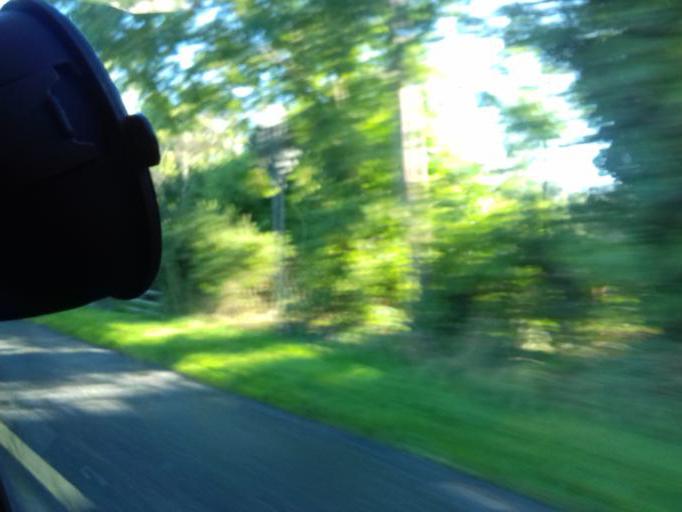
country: IE
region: Leinster
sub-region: An Iarmhi
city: Kilbeggan
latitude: 53.3317
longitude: -7.5117
